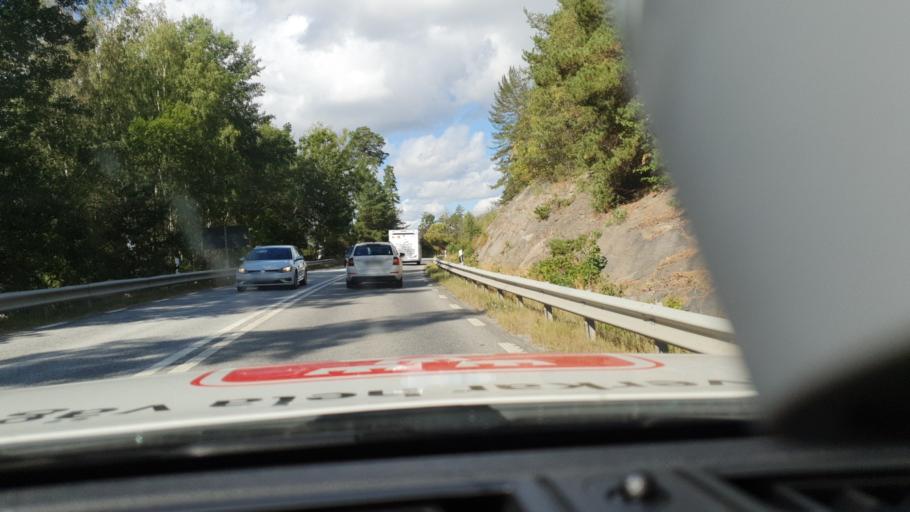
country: SE
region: Stockholm
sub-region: Vaxholms Kommun
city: Resaro
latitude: 59.4181
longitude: 18.3057
